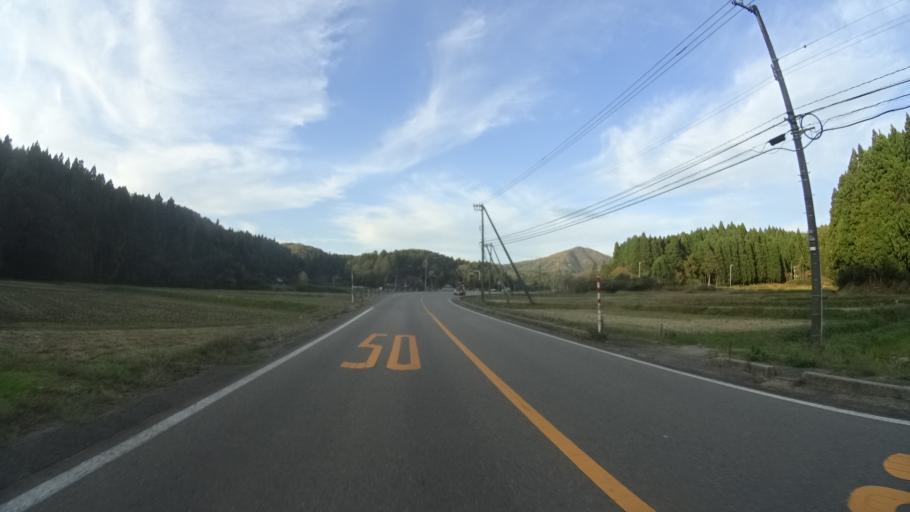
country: JP
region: Ishikawa
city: Nanao
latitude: 37.1845
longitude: 136.7142
